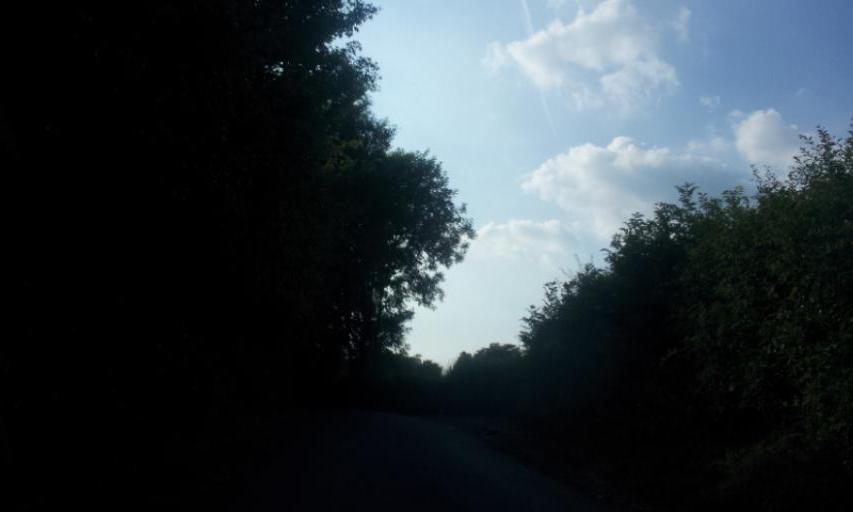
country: GB
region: England
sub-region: Kent
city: Boxley
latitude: 51.2892
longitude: 0.5949
